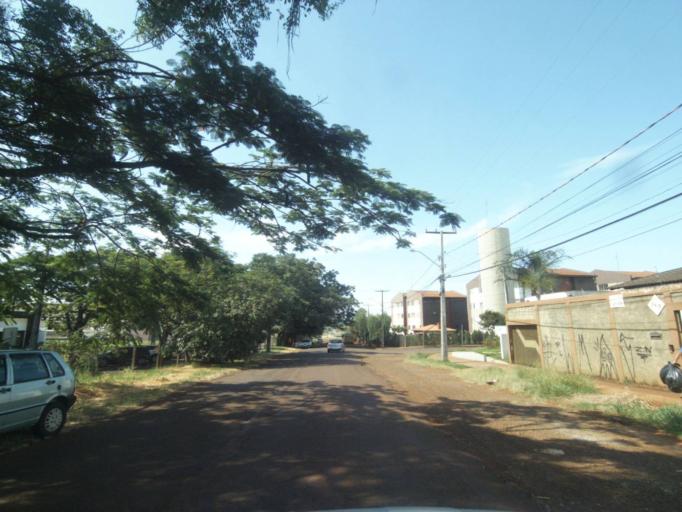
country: BR
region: Parana
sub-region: Londrina
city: Londrina
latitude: -23.3267
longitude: -51.1940
